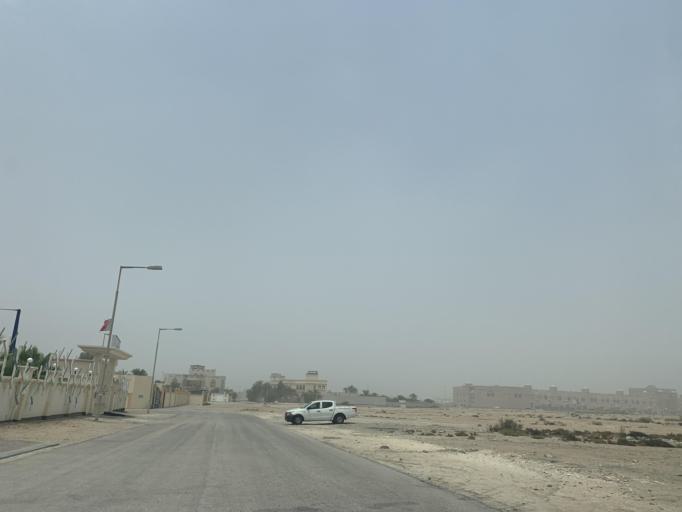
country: BH
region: Central Governorate
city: Madinat Hamad
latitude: 26.1695
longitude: 50.4744
